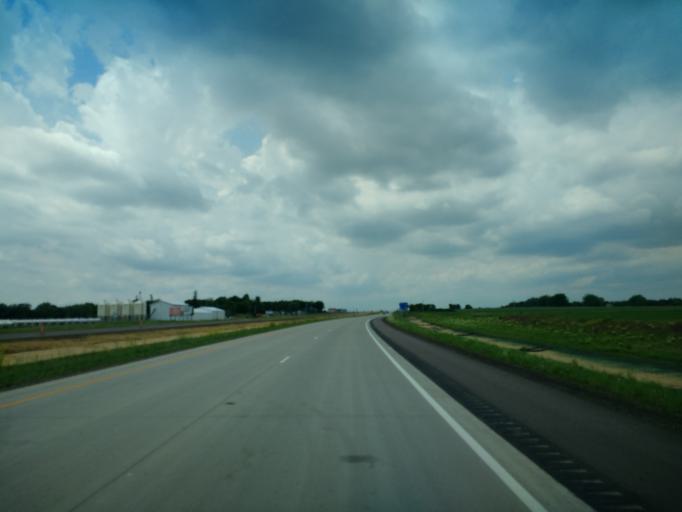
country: US
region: Minnesota
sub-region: Cottonwood County
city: Windom
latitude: 43.9103
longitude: -95.0338
